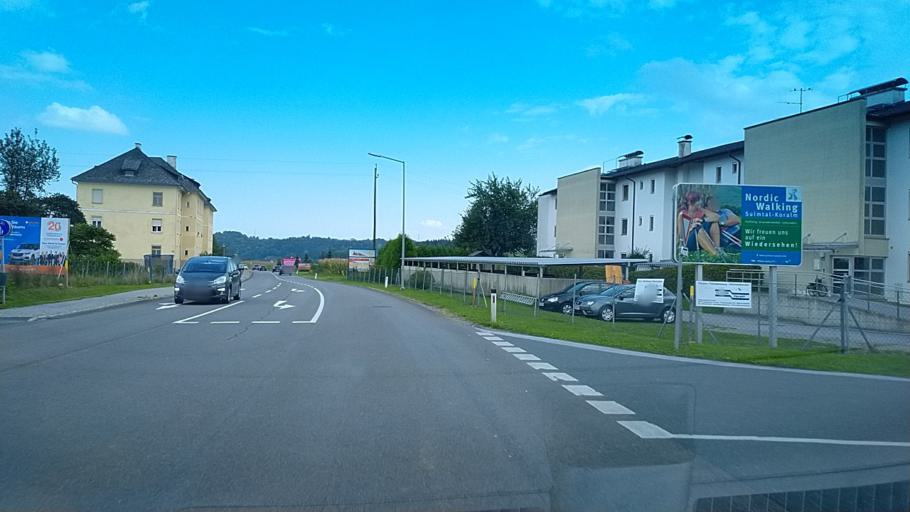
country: AT
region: Styria
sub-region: Politischer Bezirk Deutschlandsberg
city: Schwanberg
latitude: 46.7554
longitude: 15.2092
